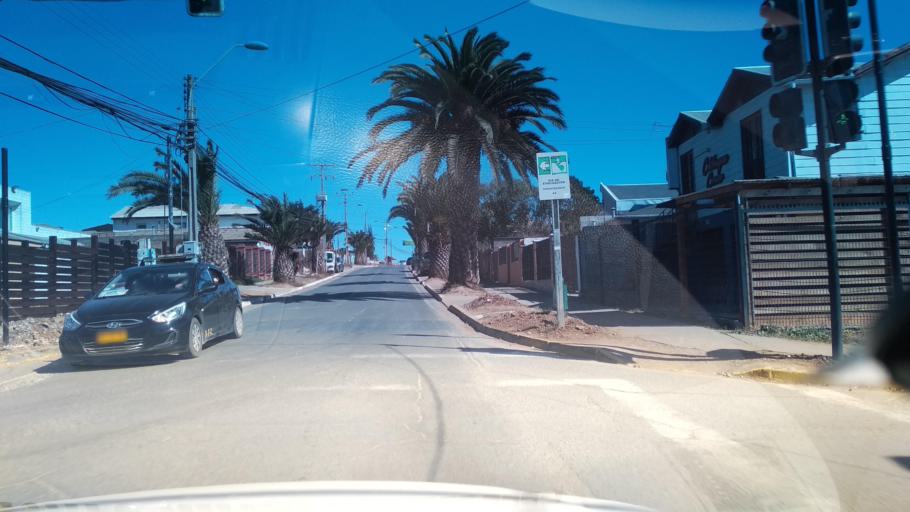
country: CL
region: O'Higgins
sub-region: Provincia de Colchagua
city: Santa Cruz
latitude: -34.3930
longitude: -72.0161
